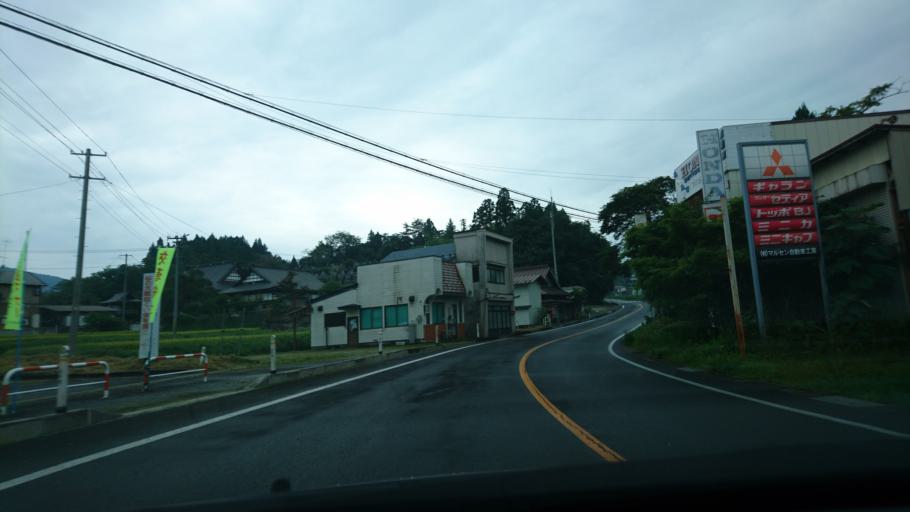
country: JP
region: Iwate
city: Ichinoseki
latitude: 39.0168
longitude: 141.2298
